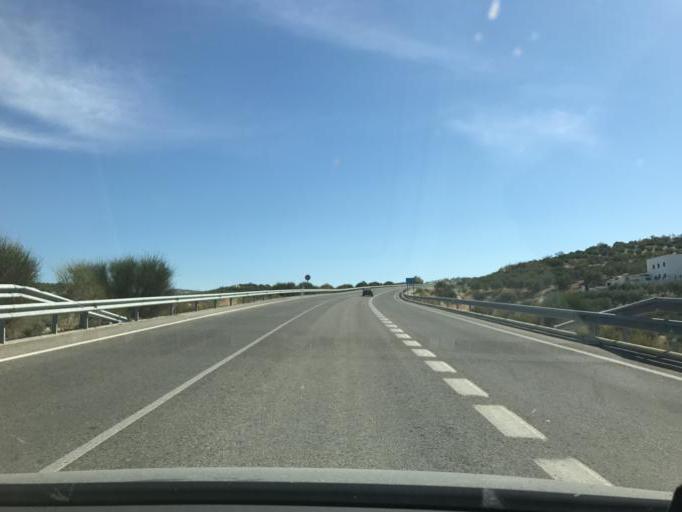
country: ES
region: Andalusia
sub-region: Province of Cordoba
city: Baena
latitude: 37.6305
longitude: -4.3152
